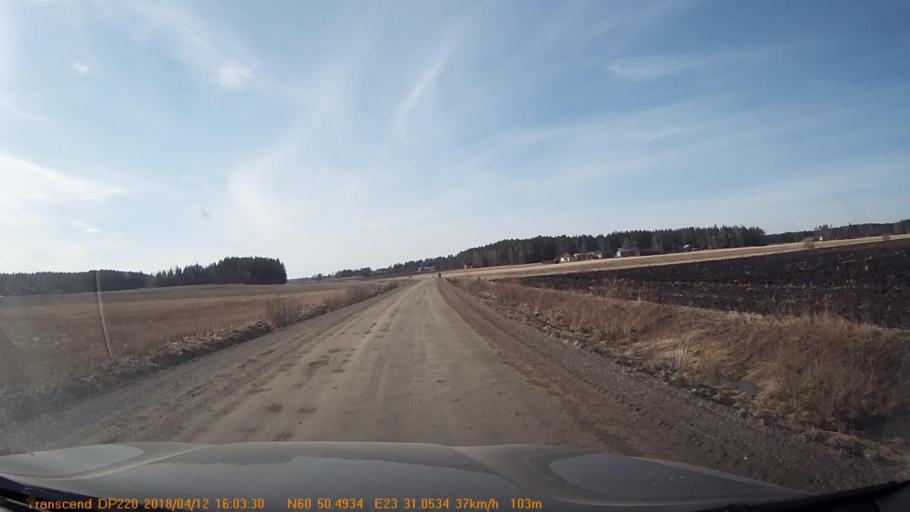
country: FI
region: Haeme
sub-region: Forssa
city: Jokioinen
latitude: 60.8417
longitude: 23.5171
